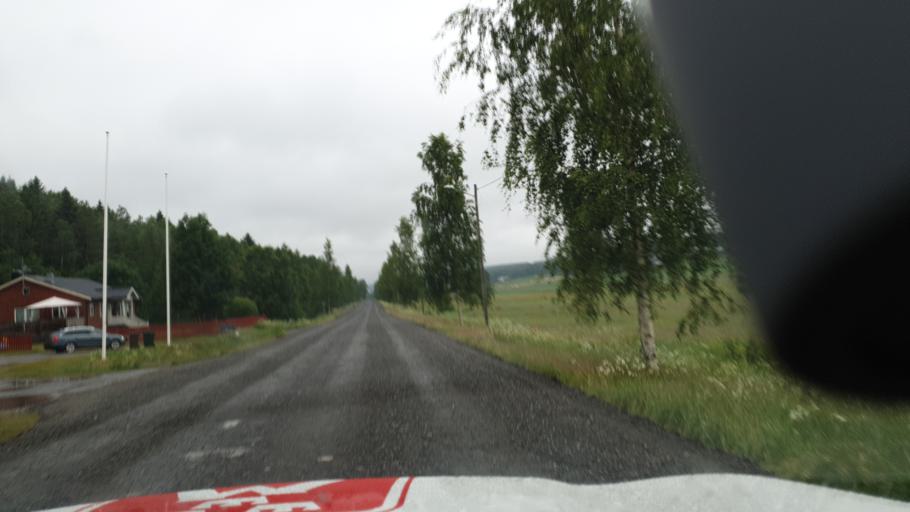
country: SE
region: Vaesterbotten
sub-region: Vannas Kommun
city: Vaennaes
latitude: 63.7445
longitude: 19.6488
